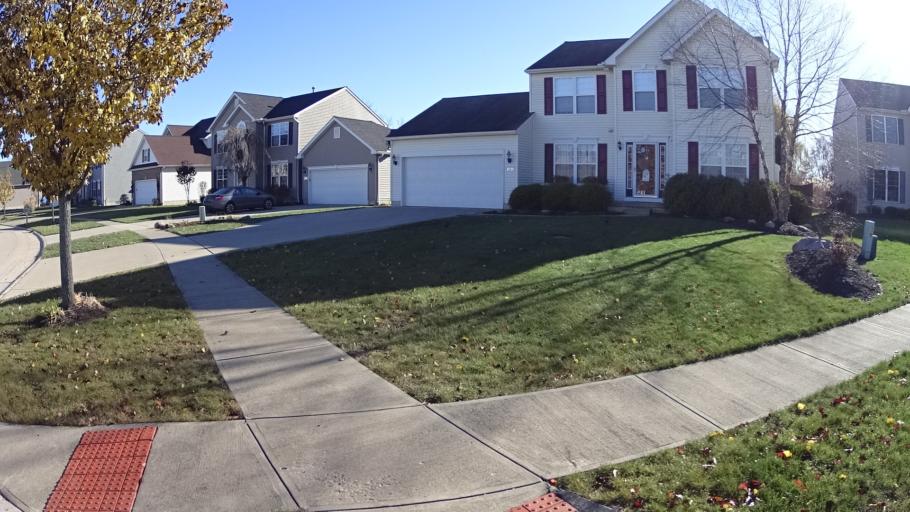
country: US
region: Ohio
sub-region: Lorain County
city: Avon Center
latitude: 41.4601
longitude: -81.9813
